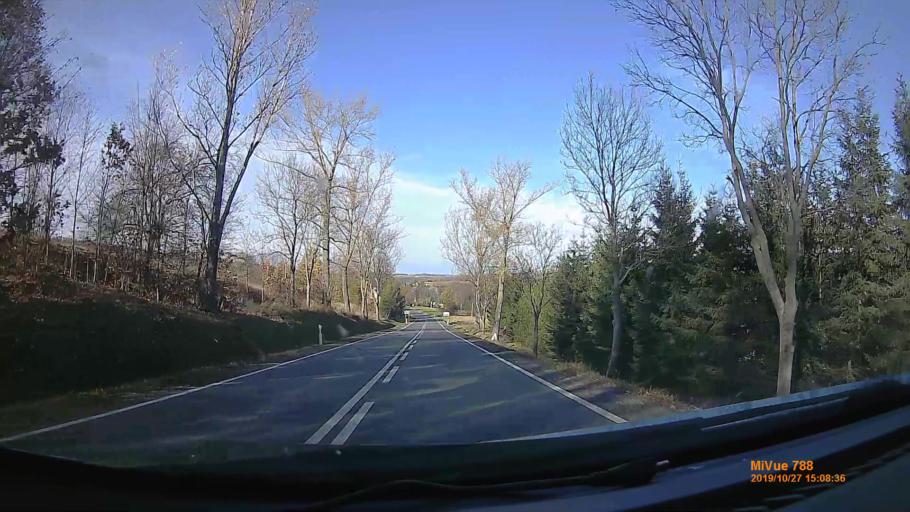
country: PL
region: Lower Silesian Voivodeship
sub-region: Powiat klodzki
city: Miedzylesie
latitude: 50.1719
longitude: 16.6698
